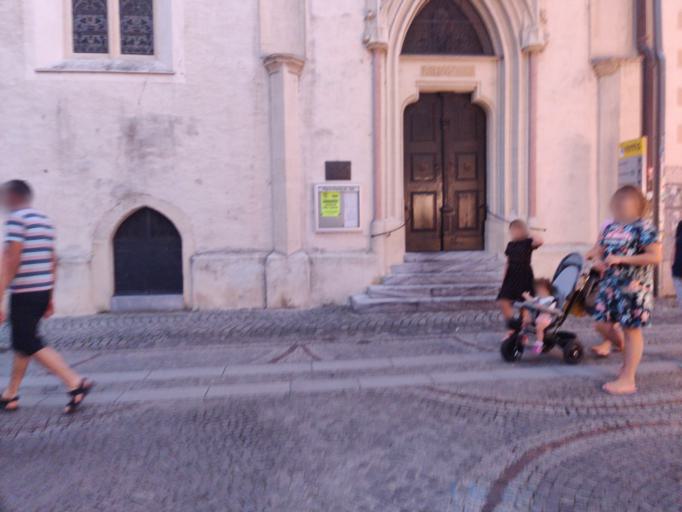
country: AT
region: Lower Austria
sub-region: Politischer Bezirk Krems
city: Weinzierl bei Krems
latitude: 48.4111
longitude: 15.5996
